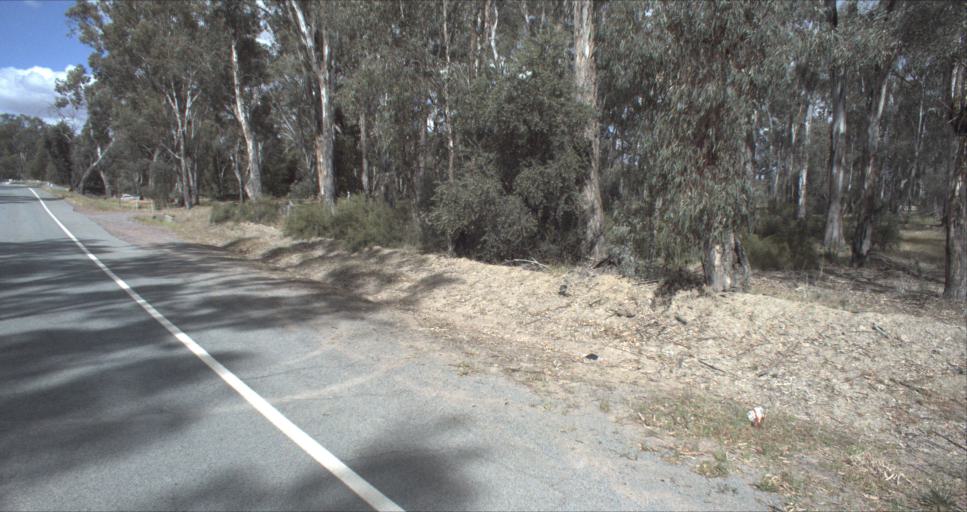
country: AU
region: New South Wales
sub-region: Leeton
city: Leeton
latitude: -34.6398
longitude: 146.3718
